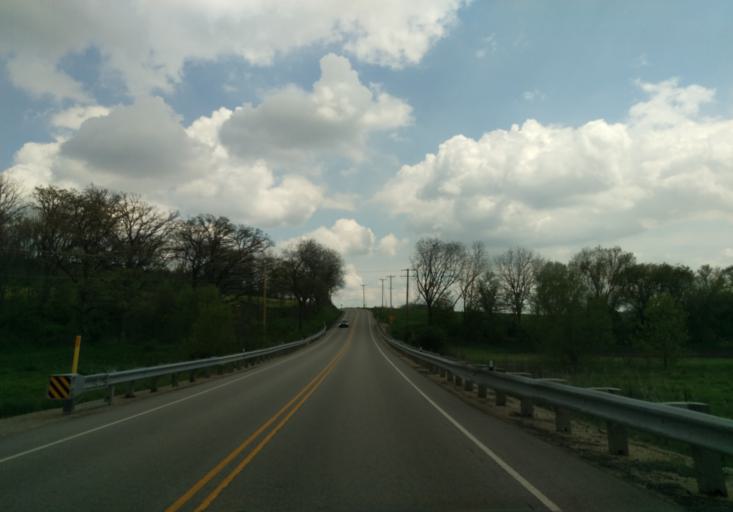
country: US
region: Wisconsin
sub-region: Dane County
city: Mount Horeb
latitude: 42.9648
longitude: -89.6929
